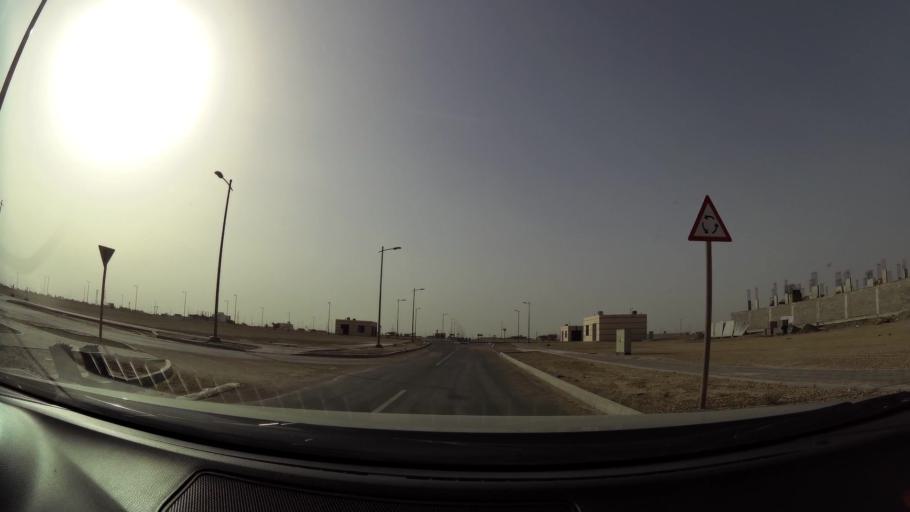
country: AE
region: Abu Dhabi
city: Al Ain
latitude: 24.1173
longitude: 55.7251
